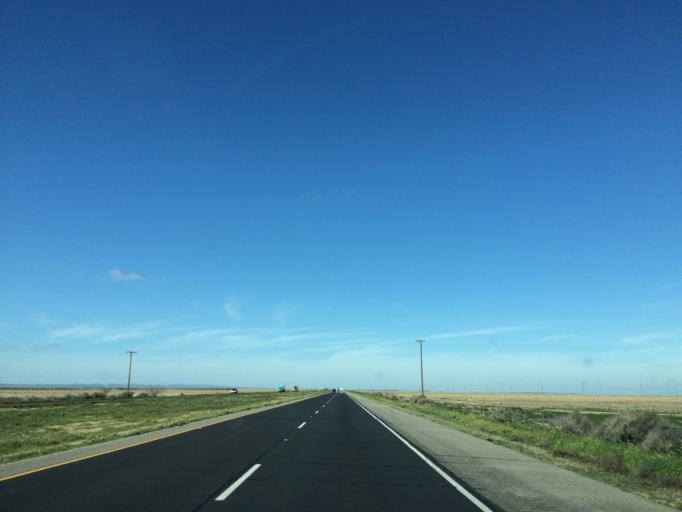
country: US
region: California
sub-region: Kern County
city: Lost Hills
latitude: 35.8033
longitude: -119.7924
